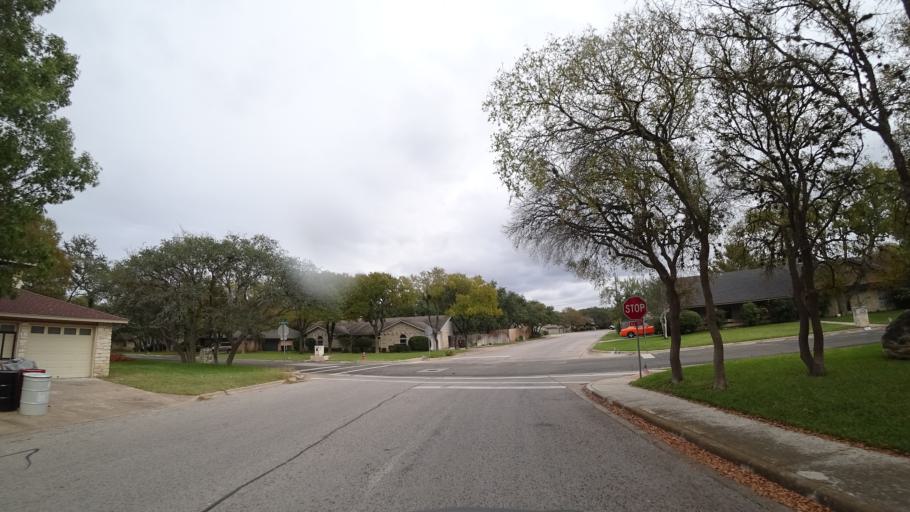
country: US
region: Texas
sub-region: Williamson County
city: Round Rock
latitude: 30.5001
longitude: -97.6929
